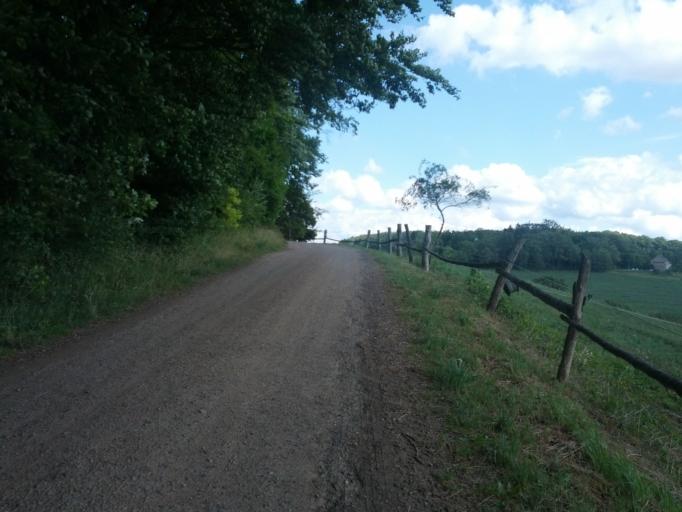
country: DE
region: Thuringia
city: Wolfsburg-Unkeroda
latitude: 50.9641
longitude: 10.2425
